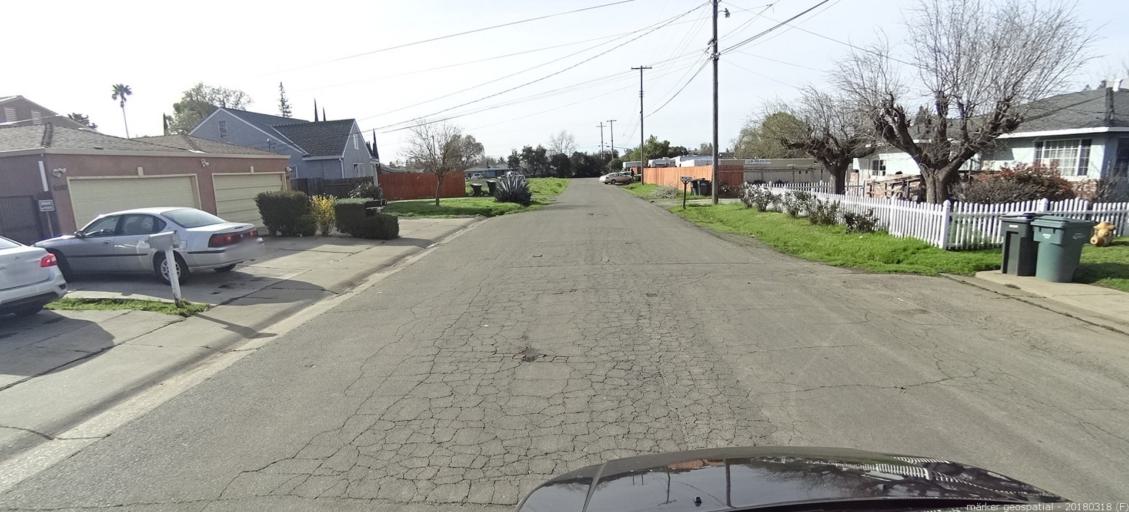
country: US
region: California
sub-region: Sacramento County
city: Parkway
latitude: 38.5075
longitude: -121.4611
